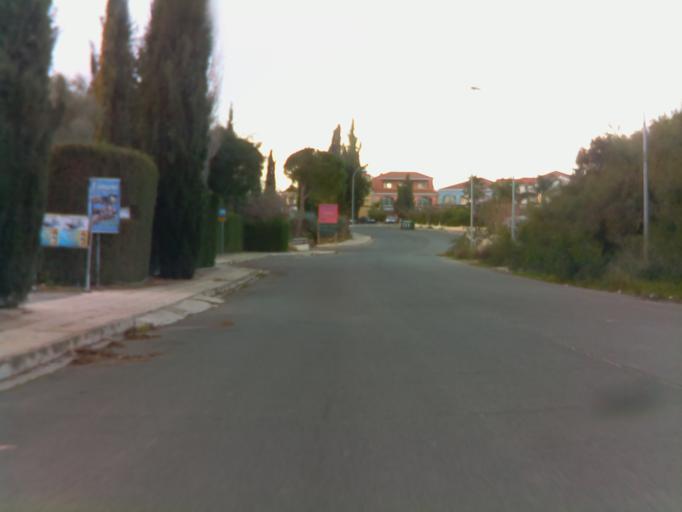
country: CY
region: Pafos
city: Pegeia
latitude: 34.8585
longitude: 32.3629
